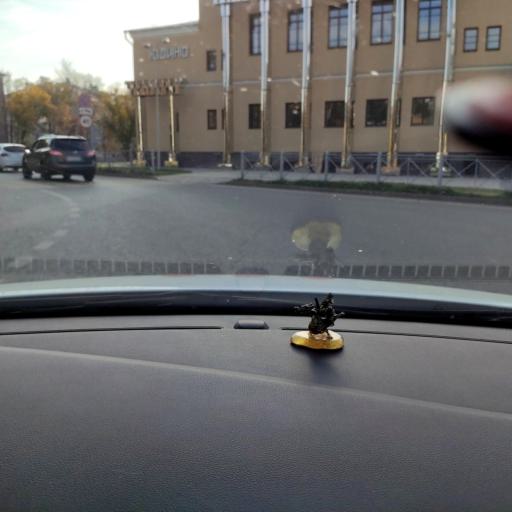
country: RU
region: Tatarstan
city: Osinovo
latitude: 55.8221
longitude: 48.8973
